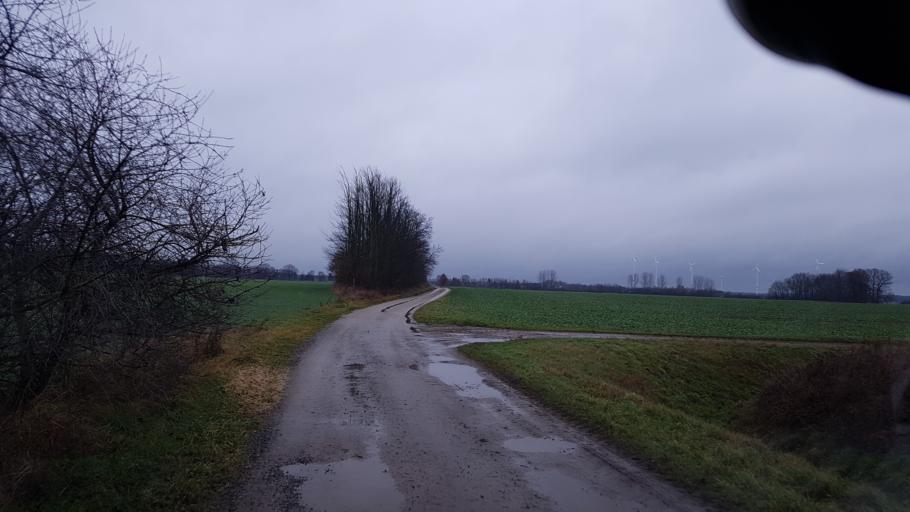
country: DE
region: Brandenburg
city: Sallgast
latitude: 51.6277
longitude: 13.8469
